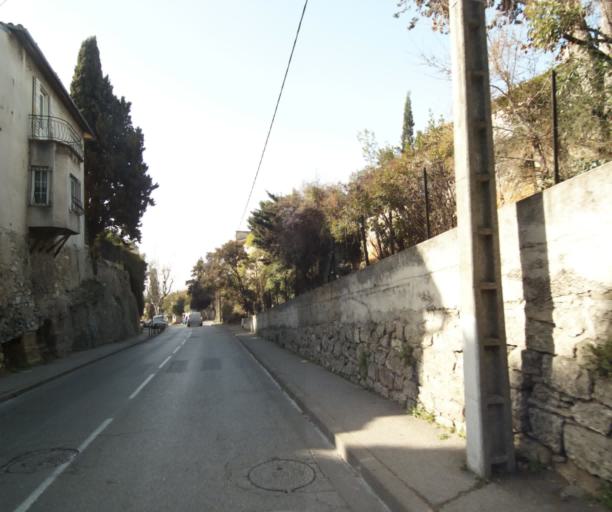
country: FR
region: Provence-Alpes-Cote d'Azur
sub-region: Departement des Bouches-du-Rhone
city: Aix-en-Provence
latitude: 43.5355
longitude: 5.4517
